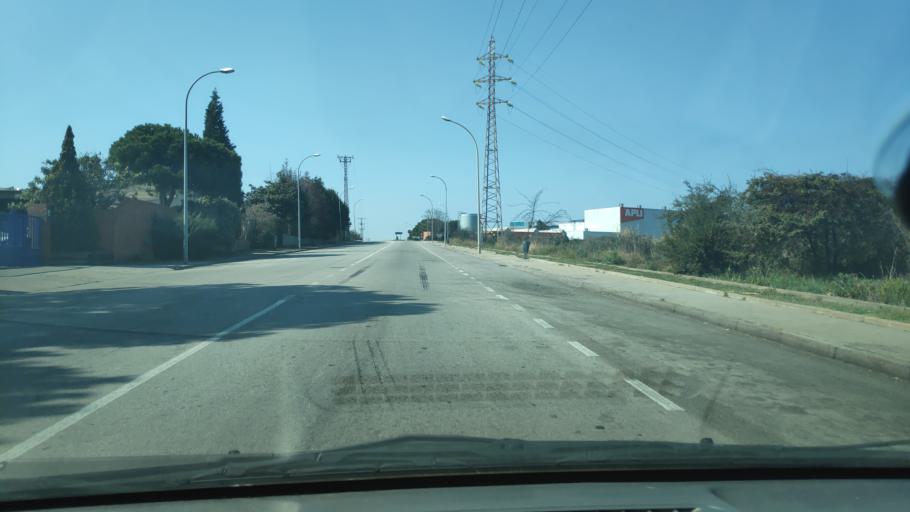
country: ES
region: Catalonia
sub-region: Provincia de Barcelona
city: Ripollet
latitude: 41.5226
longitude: 2.1508
